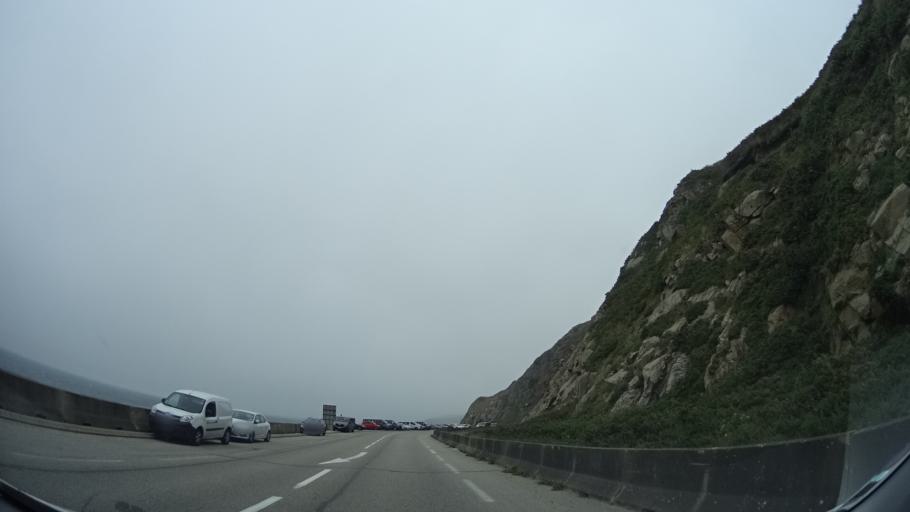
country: FR
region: Lower Normandy
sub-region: Departement de la Manche
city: Flamanville
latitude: 49.5461
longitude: -1.8714
